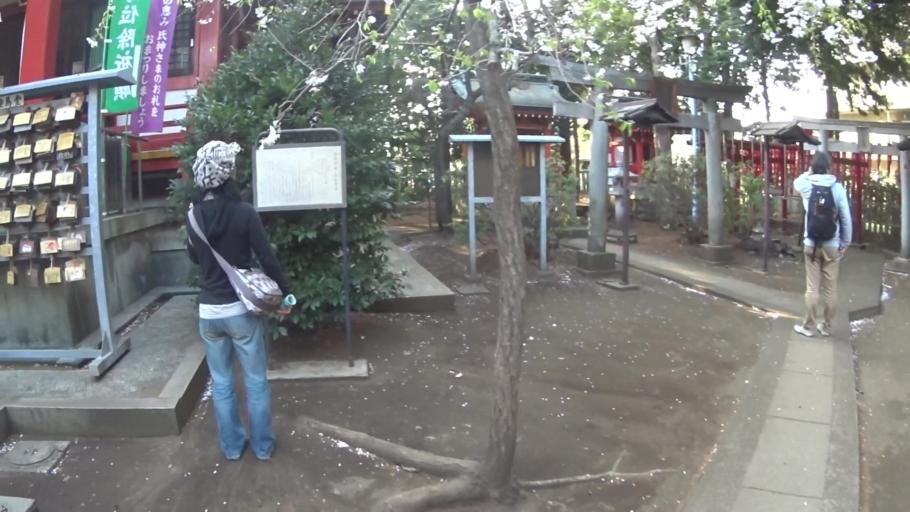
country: JP
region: Tokyo
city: Kokubunji
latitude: 35.7064
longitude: 139.5016
